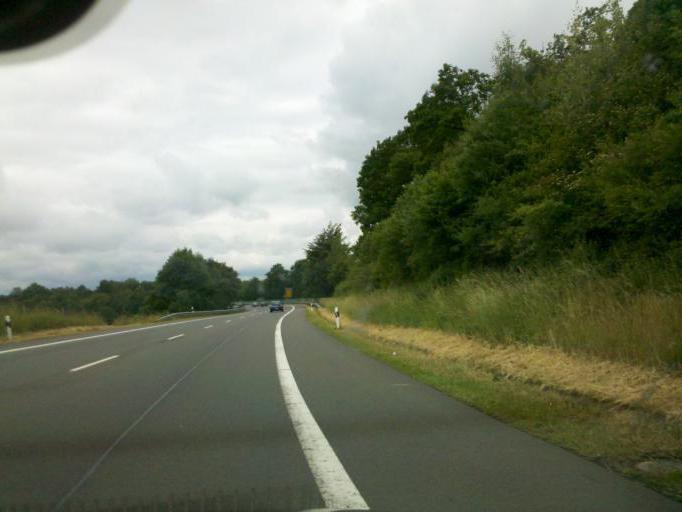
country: DE
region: North Rhine-Westphalia
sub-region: Regierungsbezirk Arnsberg
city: Olpe
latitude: 51.0460
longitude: 7.8635
